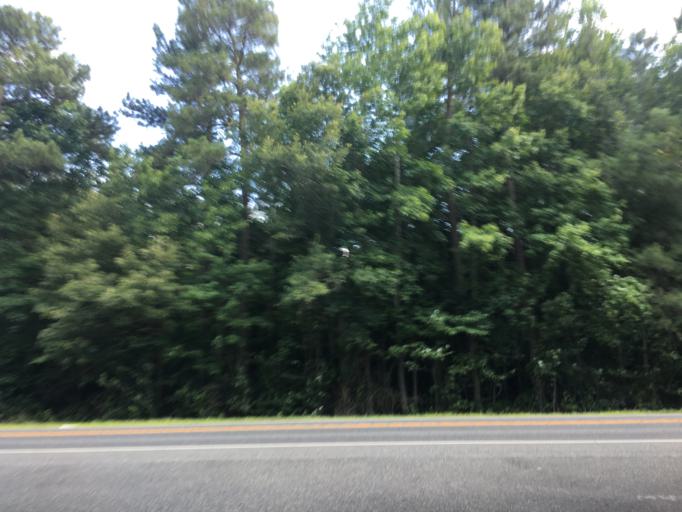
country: US
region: Delaware
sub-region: Sussex County
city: Georgetown
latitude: 38.7429
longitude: -75.4285
